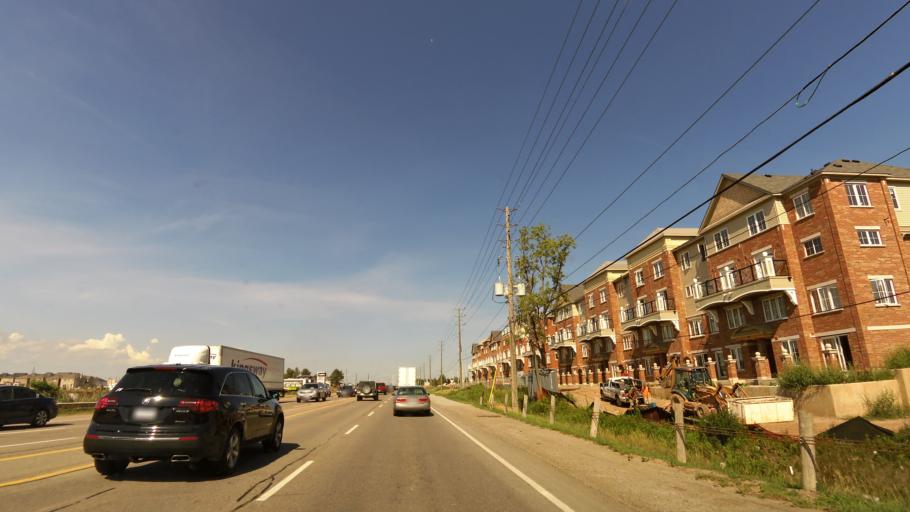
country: CA
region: Ontario
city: Oakville
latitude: 43.4798
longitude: -79.7285
